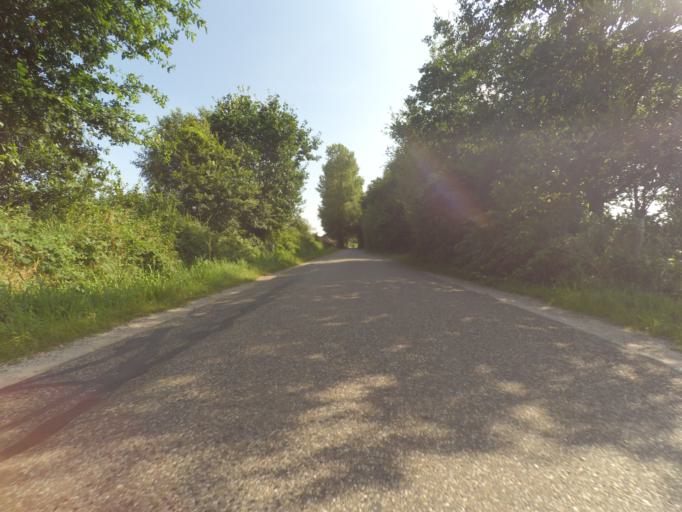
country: NL
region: Utrecht
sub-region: Gemeente Utrechtse Heuvelrug
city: Doorn
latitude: 52.0100
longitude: 5.3792
